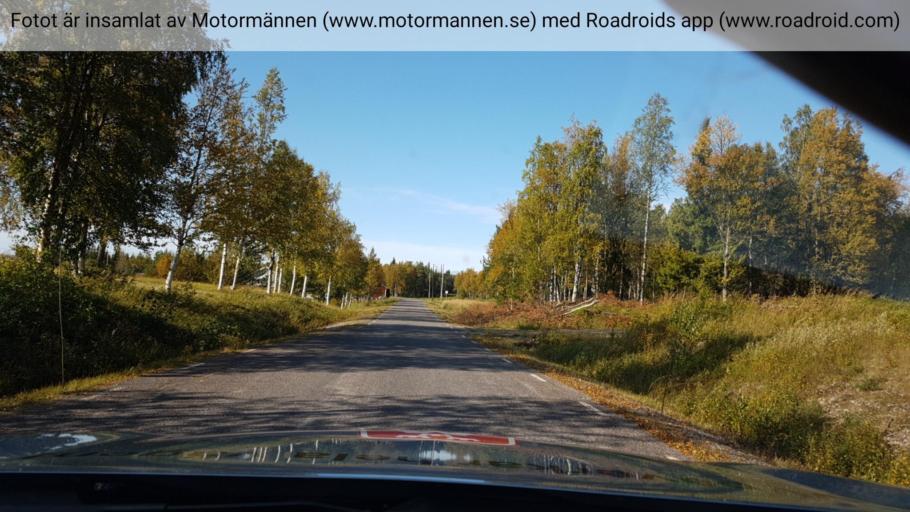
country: SE
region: Norrbotten
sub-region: Jokkmokks Kommun
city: Jokkmokk
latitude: 67.1245
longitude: 19.4988
